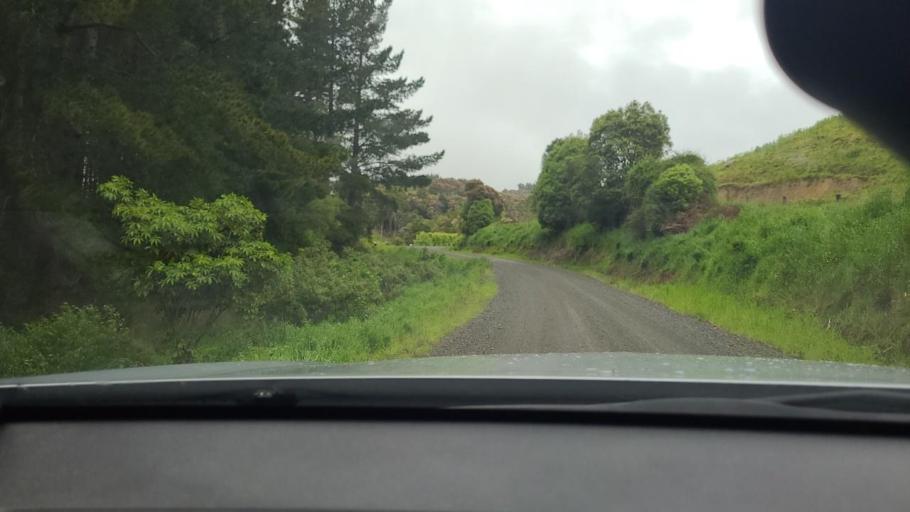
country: NZ
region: Southland
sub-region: Southland District
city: Riverton
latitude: -46.1751
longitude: 167.9898
